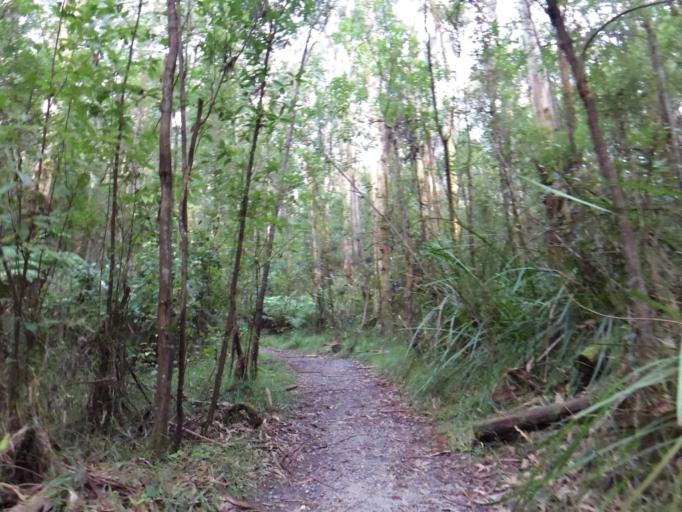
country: AU
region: Victoria
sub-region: Yarra Ranges
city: Ferny Creek
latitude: -37.8848
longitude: 145.3232
